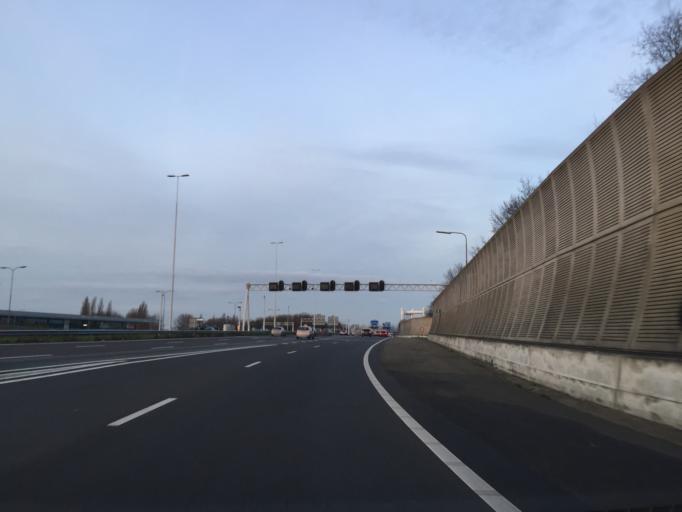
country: NL
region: South Holland
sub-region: Gemeente Zwijndrecht
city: Zwijndrecht
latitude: 51.7983
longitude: 4.6497
